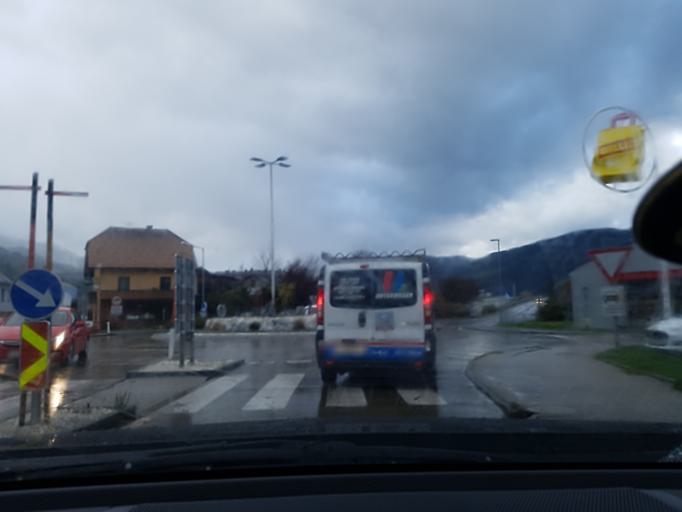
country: AT
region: Styria
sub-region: Politischer Bezirk Liezen
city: Trieben
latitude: 47.4887
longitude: 14.4855
